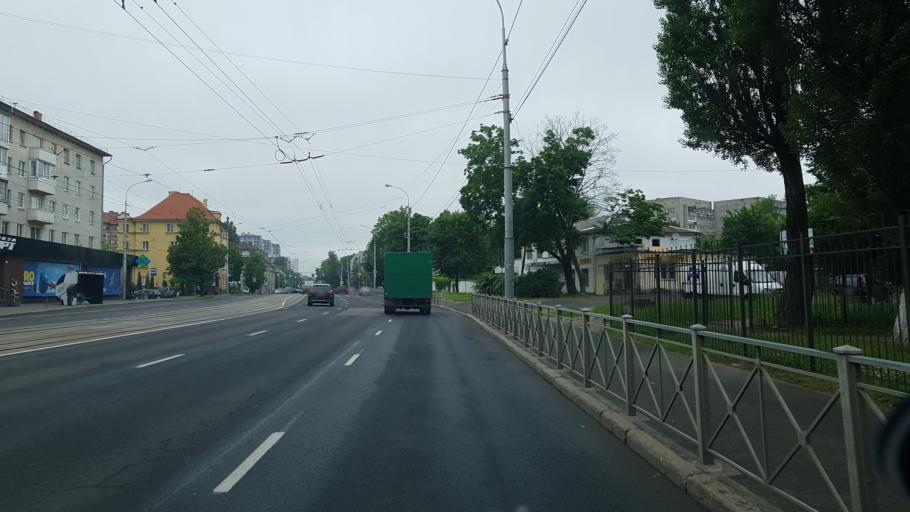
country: RU
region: Kaliningrad
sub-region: Gorod Kaliningrad
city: Kaliningrad
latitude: 54.7290
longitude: 20.4923
